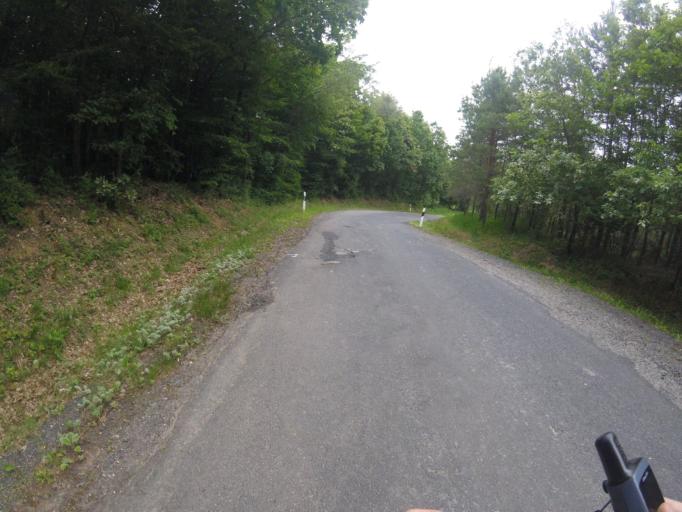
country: SI
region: Hodos-Hodos
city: Hodos
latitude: 46.8585
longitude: 16.4371
